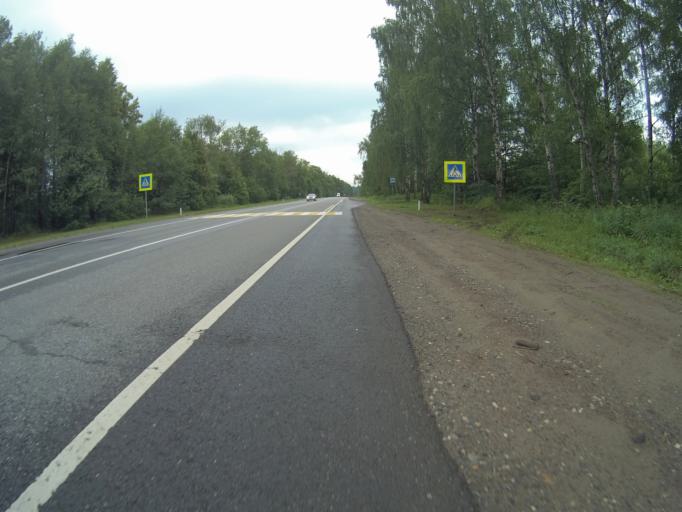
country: RU
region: Vladimir
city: Kameshkovo
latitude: 56.1967
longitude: 40.8726
